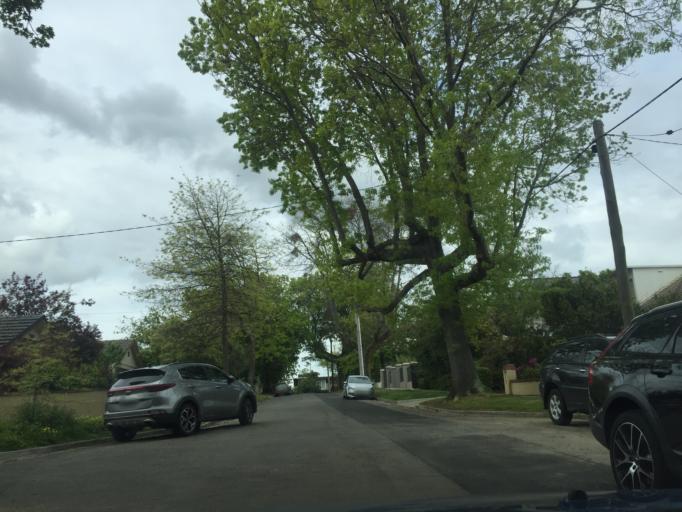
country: AU
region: Victoria
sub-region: Boroondara
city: Kew East
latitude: -37.8067
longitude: 145.0565
